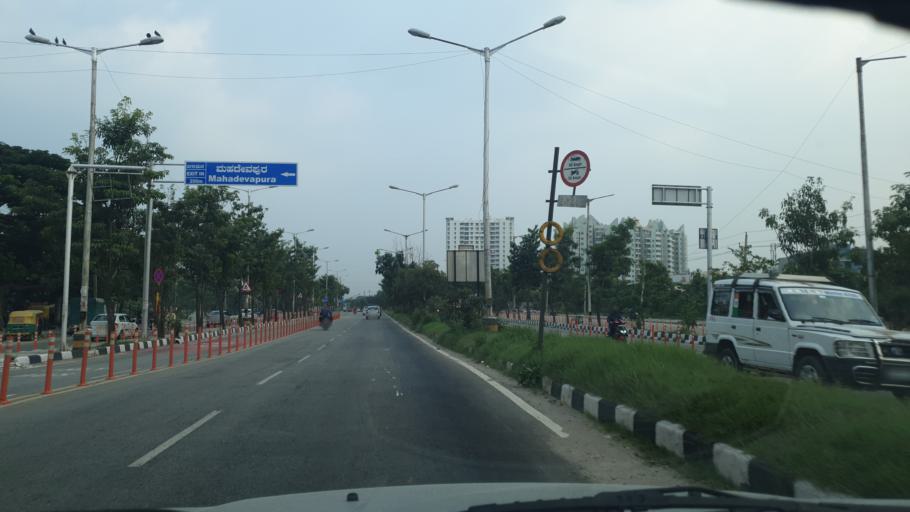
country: IN
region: Karnataka
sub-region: Bangalore Urban
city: Bangalore
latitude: 12.9979
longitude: 77.6826
